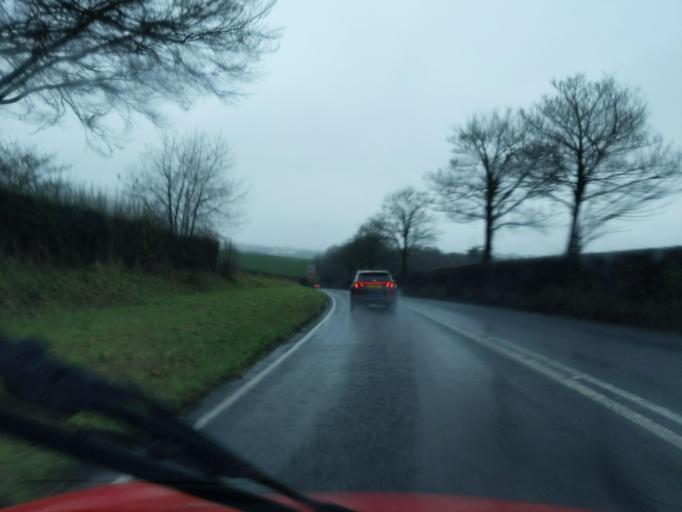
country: GB
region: England
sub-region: Cornwall
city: South Hill
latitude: 50.5547
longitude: -4.3307
